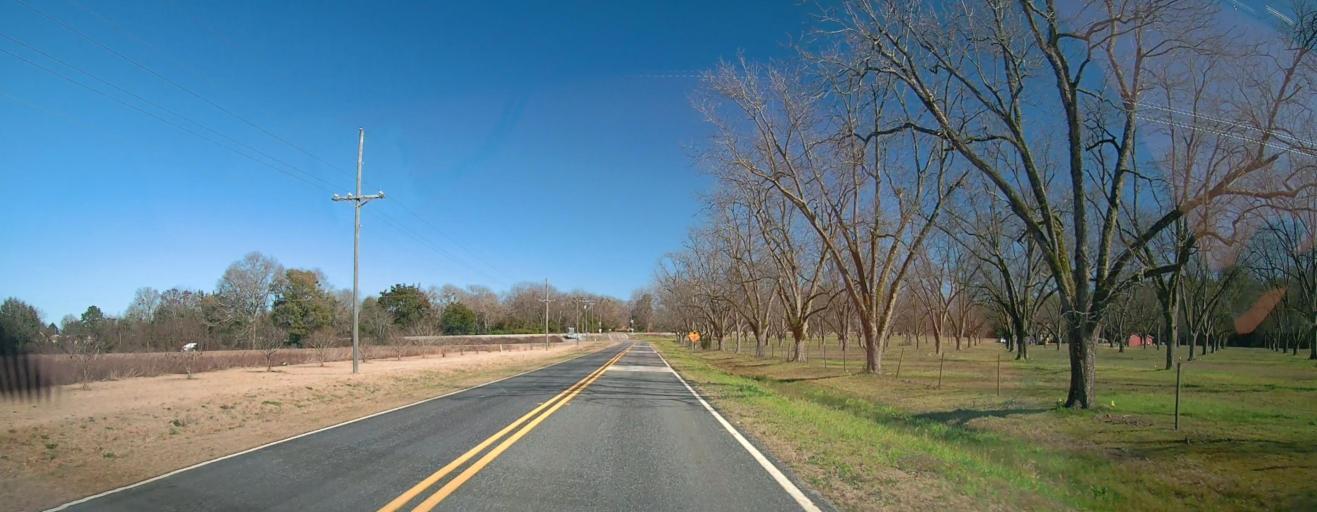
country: US
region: Georgia
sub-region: Macon County
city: Montezuma
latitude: 32.2787
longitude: -84.0045
